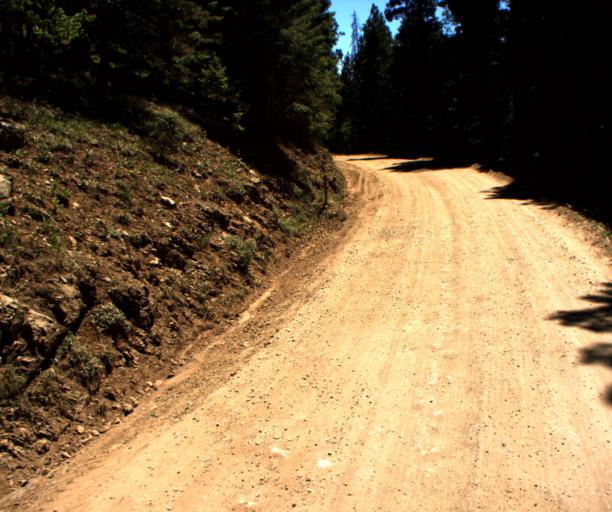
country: US
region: Arizona
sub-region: Graham County
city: Swift Trail Junction
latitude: 32.6921
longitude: -109.9002
